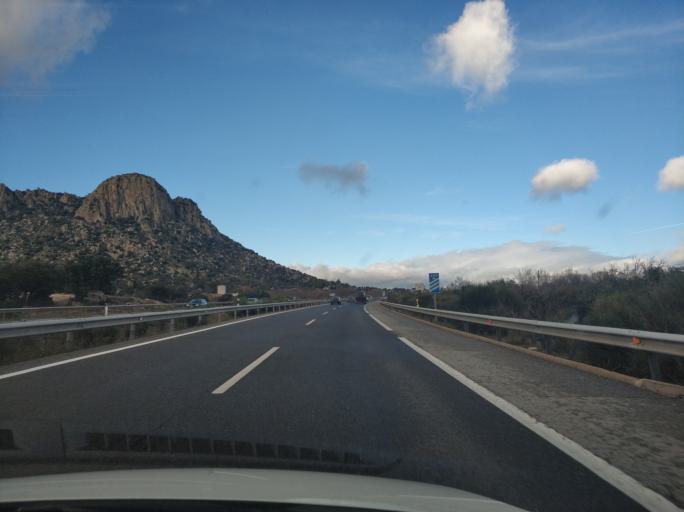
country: ES
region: Madrid
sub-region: Provincia de Madrid
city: La Cabrera
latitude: 40.8678
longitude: -3.6056
